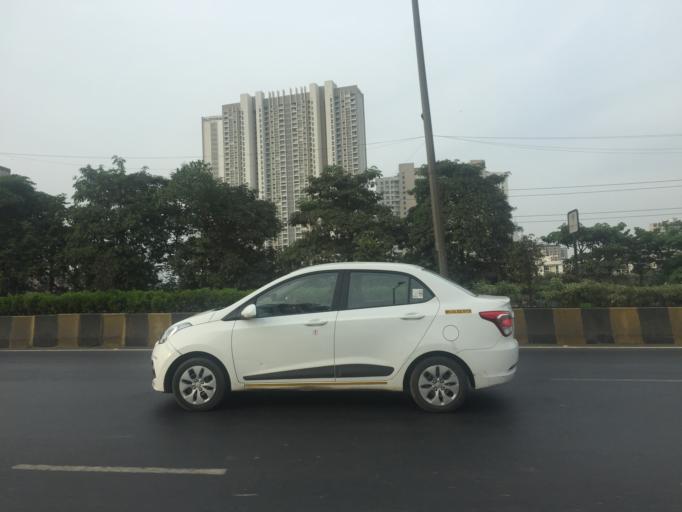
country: IN
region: Maharashtra
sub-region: Mumbai Suburban
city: Powai
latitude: 19.1249
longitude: 72.9301
